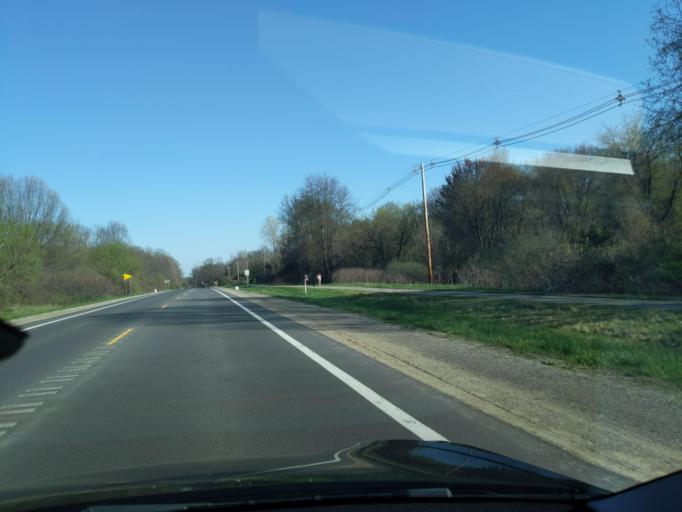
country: US
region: Michigan
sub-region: Washtenaw County
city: Chelsea
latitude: 42.3429
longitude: -84.0375
